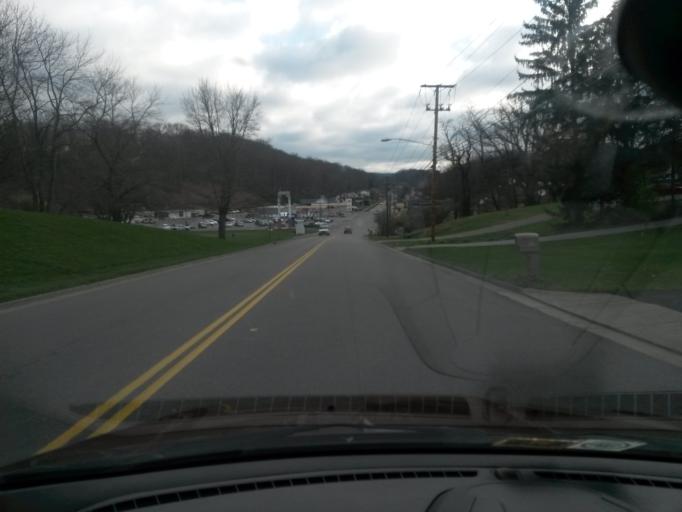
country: US
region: Virginia
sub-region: Tazewell County
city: Bluefield
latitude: 37.2449
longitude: -81.2442
